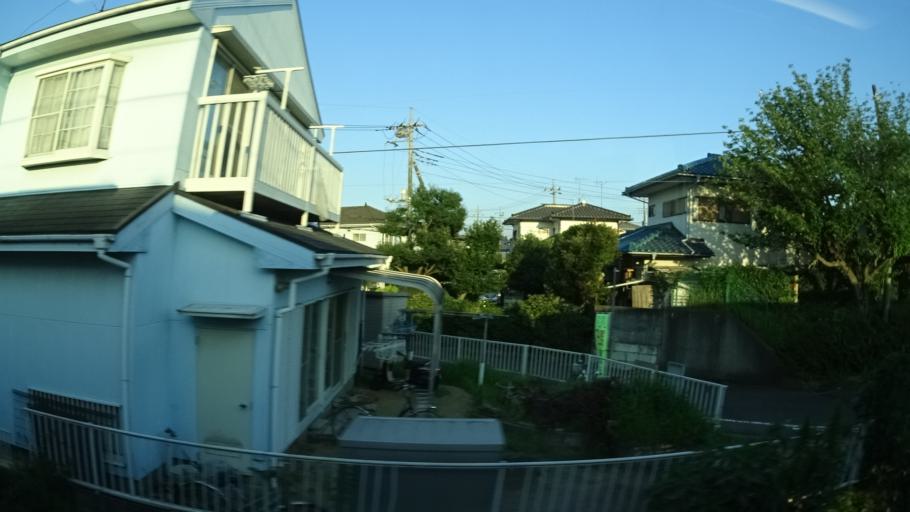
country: JP
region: Ibaraki
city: Ushiku
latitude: 35.9913
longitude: 140.1484
